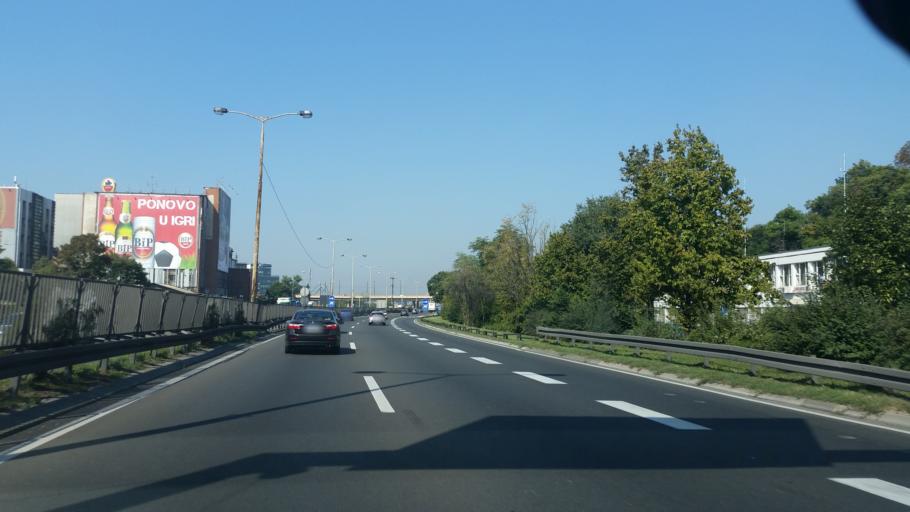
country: RS
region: Central Serbia
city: Belgrade
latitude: 44.7962
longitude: 20.4549
